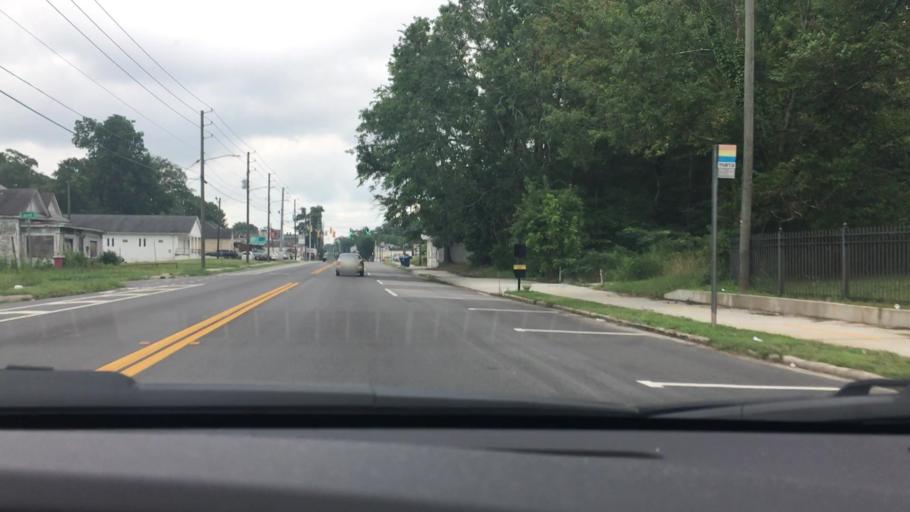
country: US
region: Georgia
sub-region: Fulton County
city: Atlanta
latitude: 33.7462
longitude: -84.4406
